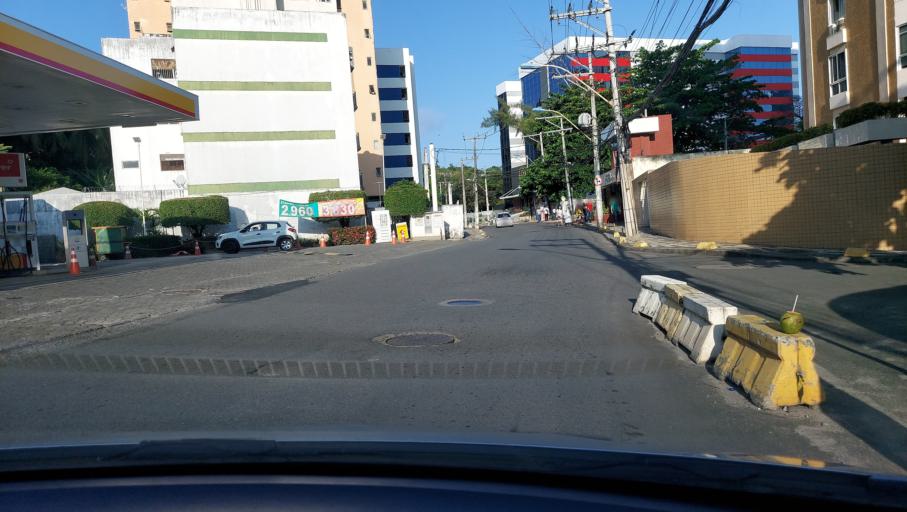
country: BR
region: Bahia
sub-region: Salvador
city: Salvador
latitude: -12.9887
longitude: -38.4469
